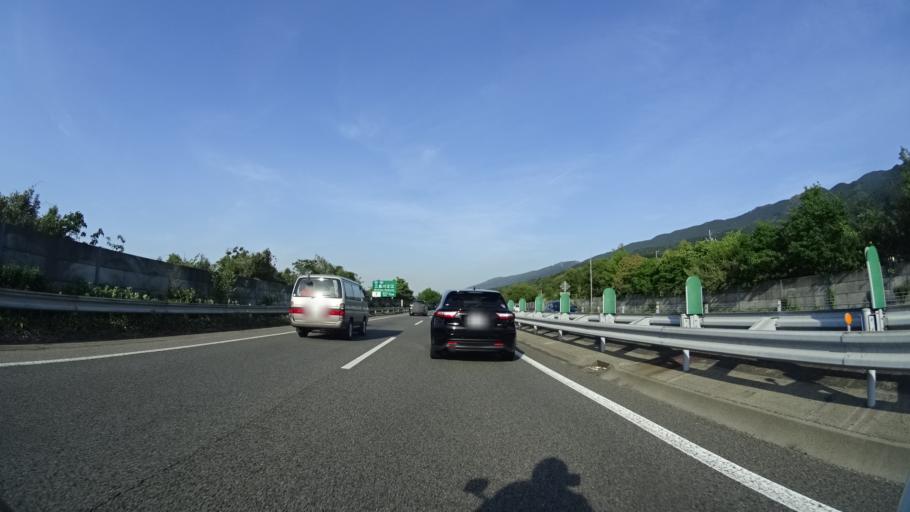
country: JP
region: Ehime
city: Kawanoecho
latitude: 33.9759
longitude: 133.5630
